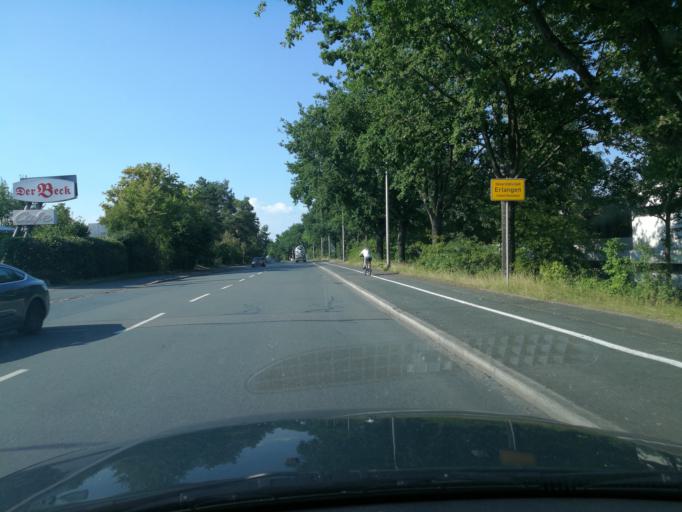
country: DE
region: Bavaria
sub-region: Regierungsbezirk Mittelfranken
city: Erlangen
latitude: 49.5773
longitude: 10.9675
